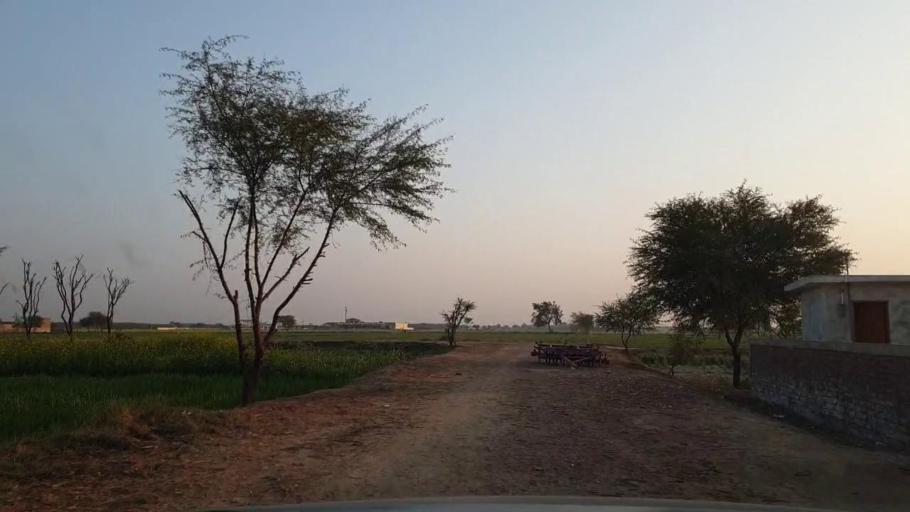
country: PK
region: Sindh
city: Tando Adam
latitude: 25.7148
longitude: 68.5762
